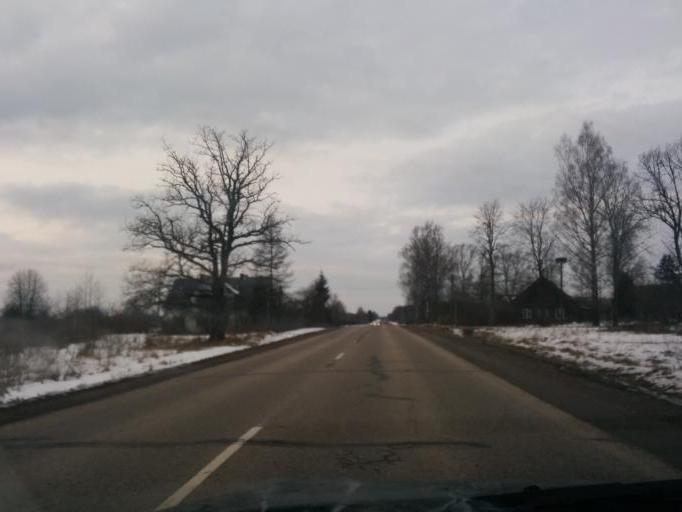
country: LV
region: Balvu Rajons
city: Balvi
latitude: 57.1469
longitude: 27.2338
